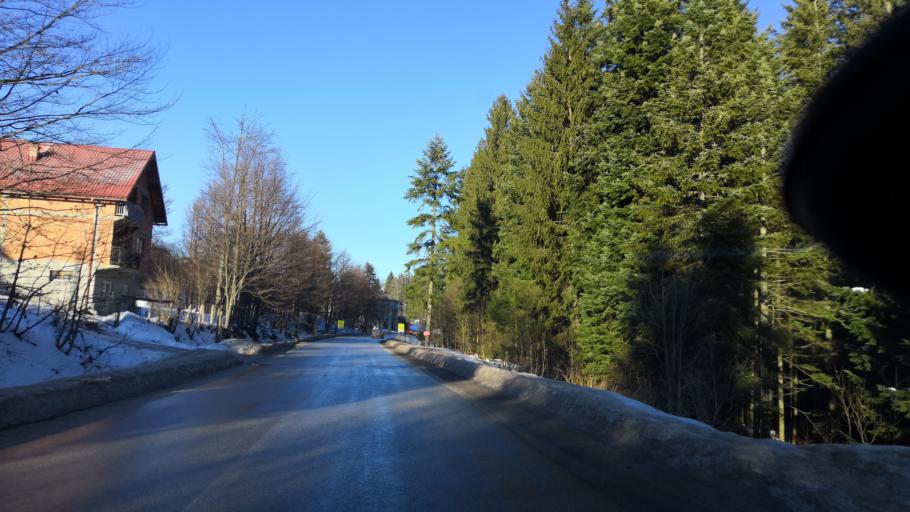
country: BA
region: Republika Srpska
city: Han Pijesak
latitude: 44.0748
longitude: 18.9500
